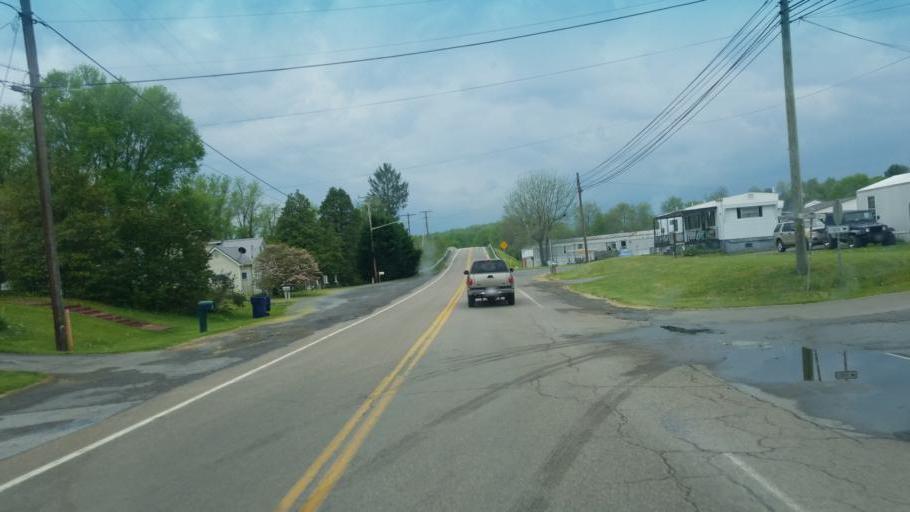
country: US
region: Virginia
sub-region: Smyth County
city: Chilhowie
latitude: 36.7917
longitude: -81.6942
